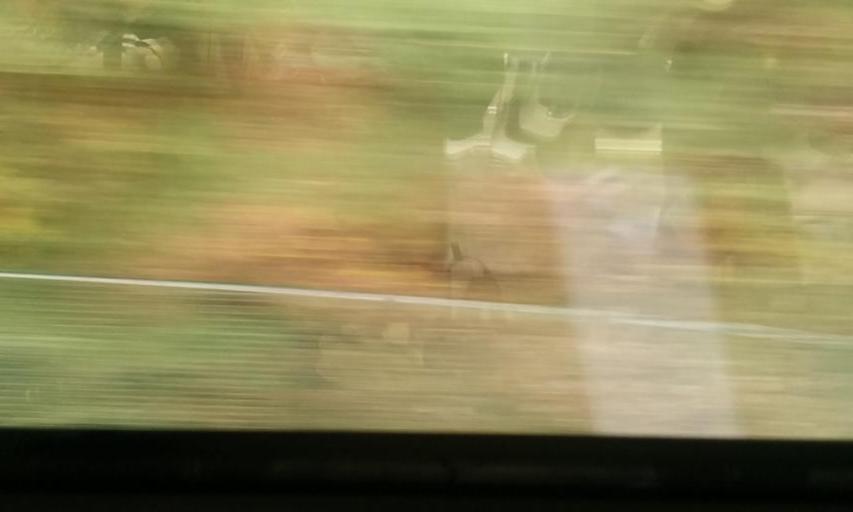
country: JP
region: Nagano
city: Iida
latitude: 35.7278
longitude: 137.7149
